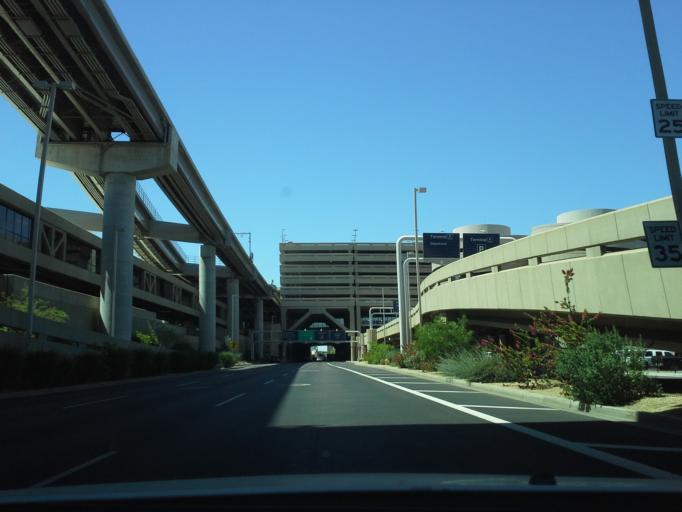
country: US
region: Arizona
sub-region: Maricopa County
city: Tempe Junction
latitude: 33.4350
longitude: -111.9943
